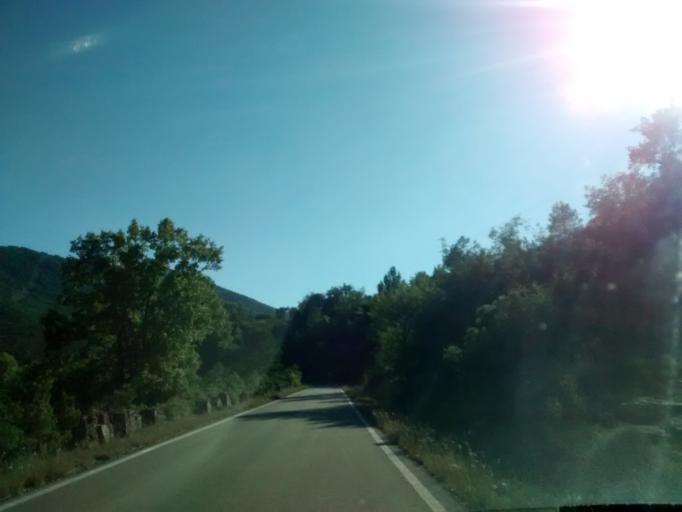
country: ES
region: Aragon
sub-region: Provincia de Huesca
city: Loarre
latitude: 42.4106
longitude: -0.6458
